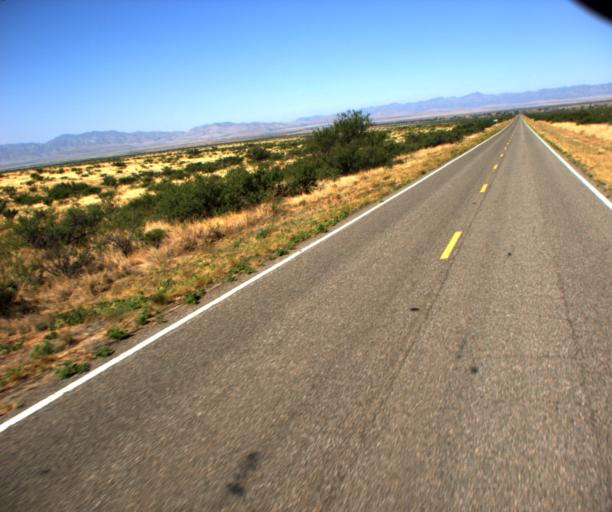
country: US
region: Arizona
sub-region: Graham County
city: Swift Trail Junction
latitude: 32.5867
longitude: -109.9222
